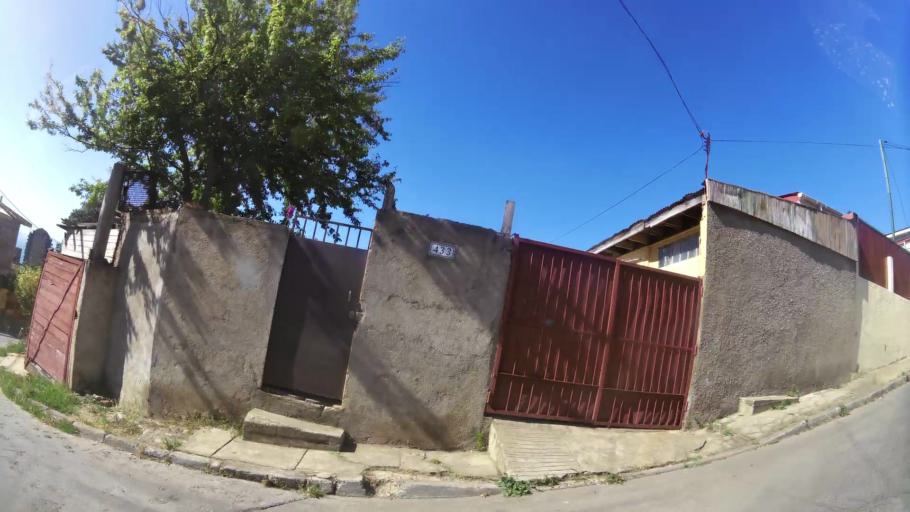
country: CL
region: Valparaiso
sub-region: Provincia de Valparaiso
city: Vina del Mar
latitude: -33.0396
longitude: -71.5644
